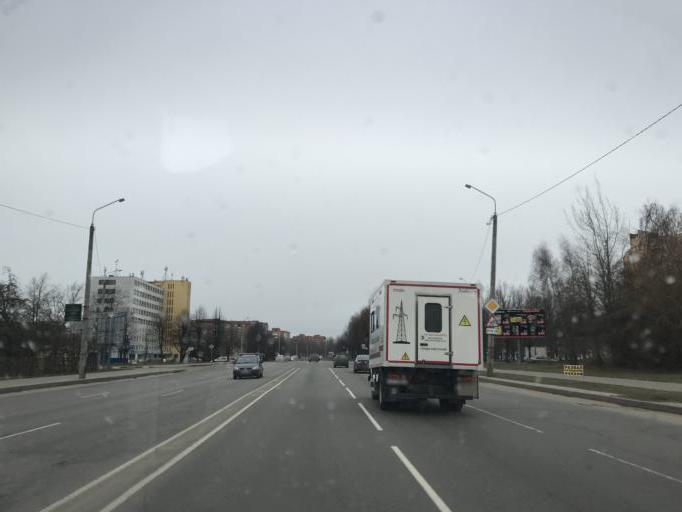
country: BY
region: Mogilev
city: Mahilyow
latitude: 53.9082
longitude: 30.3630
